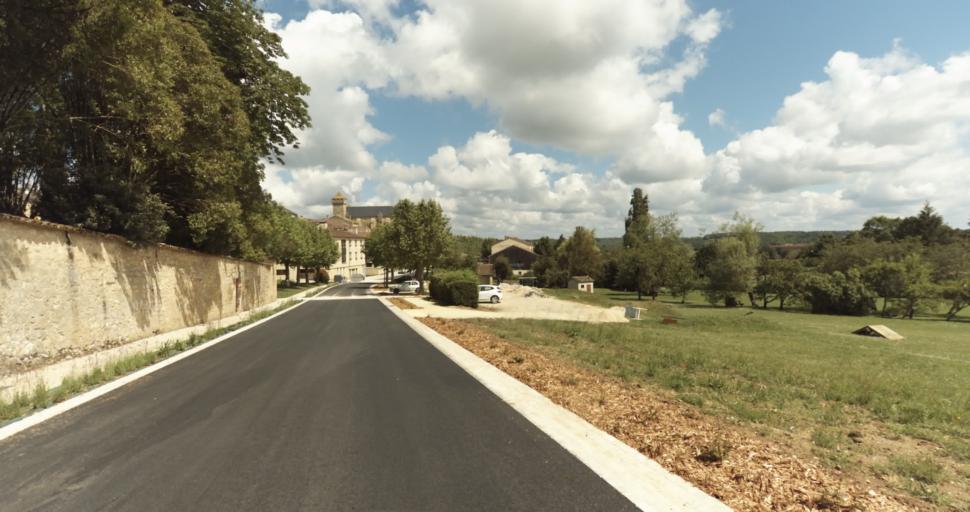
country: FR
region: Aquitaine
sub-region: Departement de la Dordogne
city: Beaumont-du-Perigord
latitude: 44.7670
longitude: 0.7689
